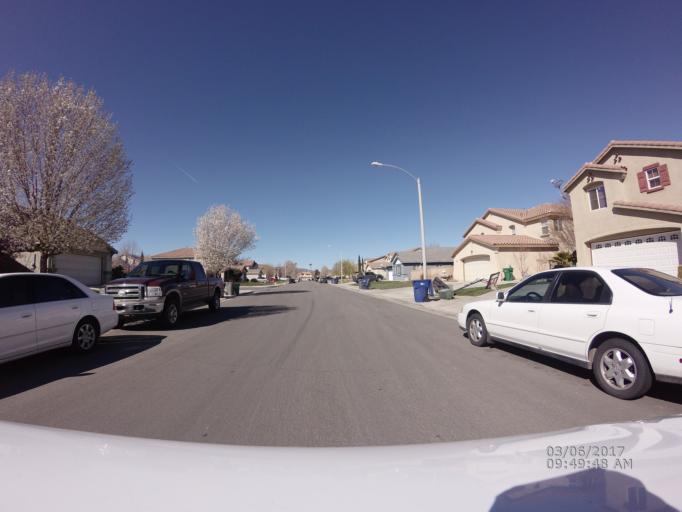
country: US
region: California
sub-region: Los Angeles County
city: Quartz Hill
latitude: 34.6504
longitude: -118.2070
